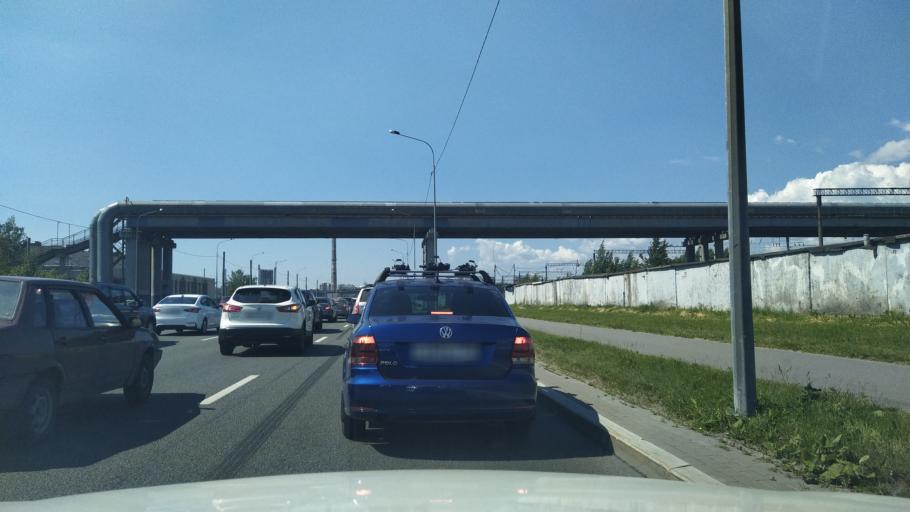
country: RU
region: Leningrad
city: Parnas
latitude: 60.0590
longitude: 30.3495
